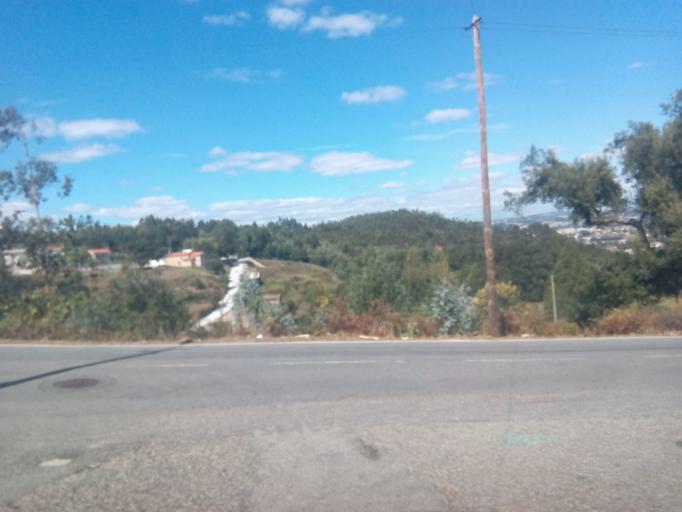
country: PT
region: Porto
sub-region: Paredes
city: Casteloes de Cepeda
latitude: 41.1544
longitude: -8.3169
